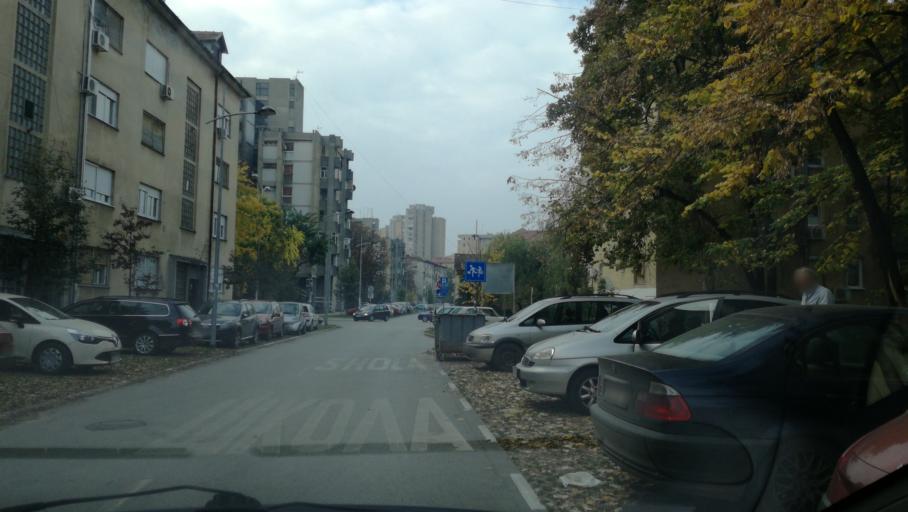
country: RS
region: Autonomna Pokrajina Vojvodina
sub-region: Juznobacki Okrug
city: Novi Sad
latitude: 45.2445
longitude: 19.8359
